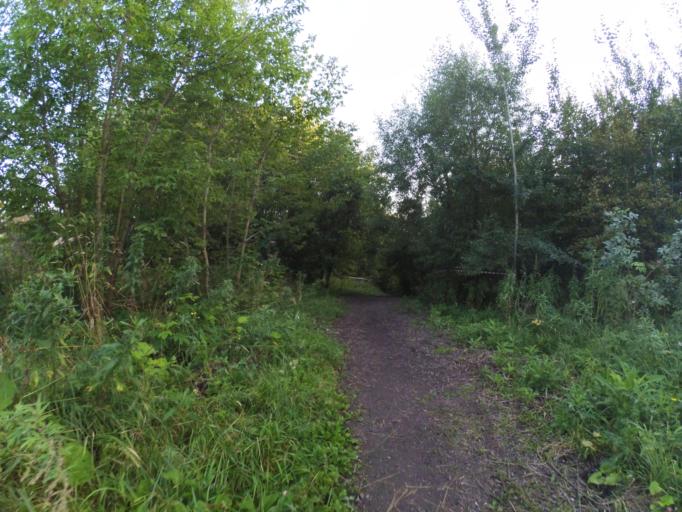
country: RU
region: Moscow
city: Khimki
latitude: 55.8623
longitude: 37.4097
